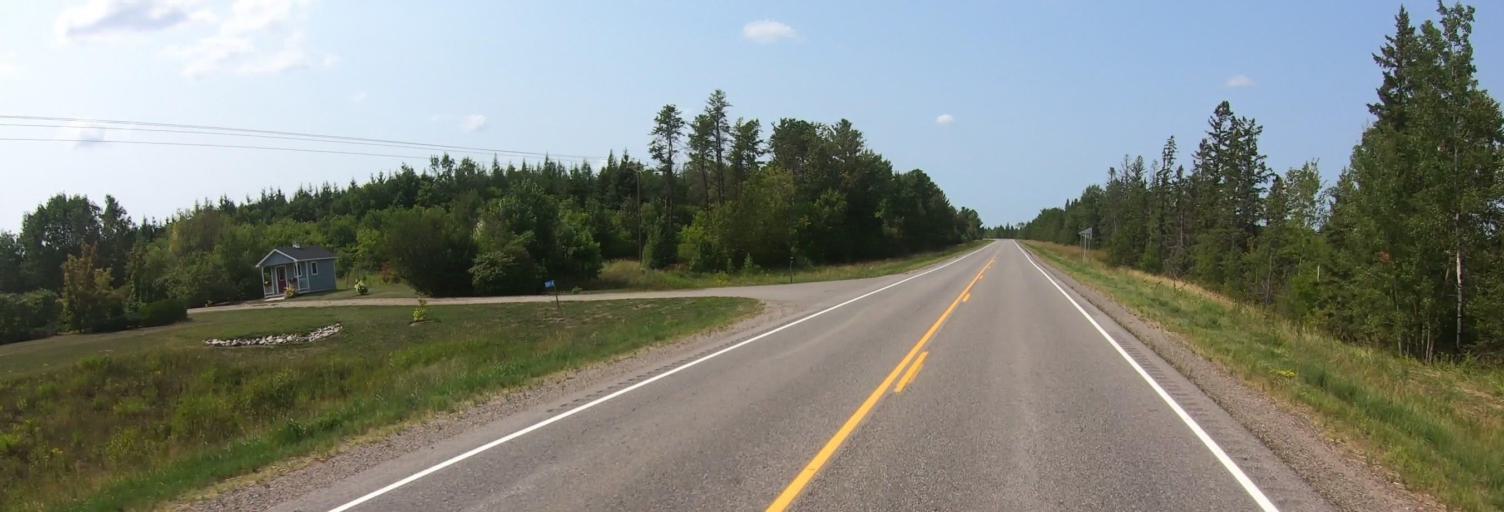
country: US
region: Minnesota
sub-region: Lake of the Woods County
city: Baudette
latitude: 48.6441
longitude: -94.1580
